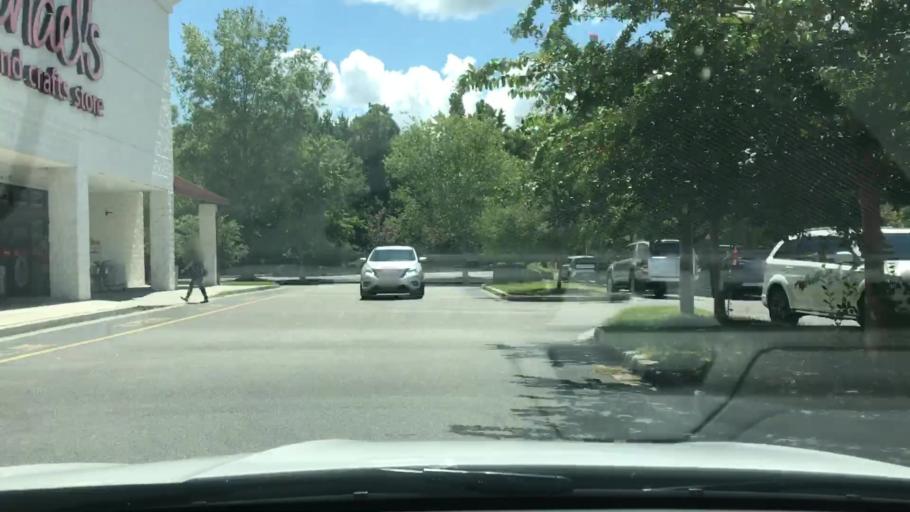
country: US
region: South Carolina
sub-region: Charleston County
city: North Charleston
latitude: 32.7945
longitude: -80.0268
